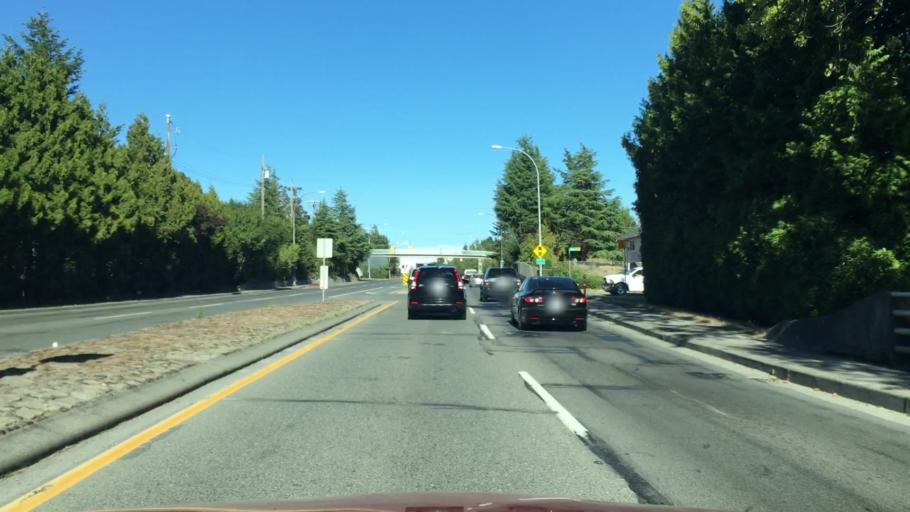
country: CA
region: British Columbia
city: Victoria
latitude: 48.4663
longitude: -123.3949
